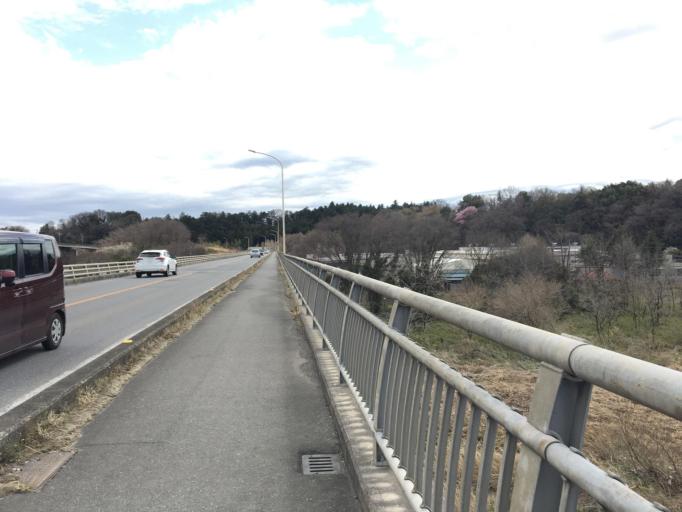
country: JP
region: Saitama
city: Yorii
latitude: 36.1179
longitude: 139.2424
